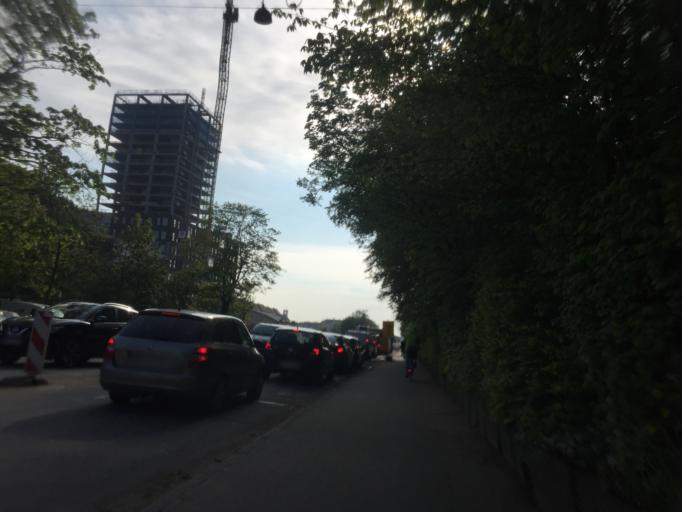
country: DK
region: Capital Region
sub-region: Frederiksberg Kommune
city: Frederiksberg
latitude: 55.6631
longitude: 12.5324
